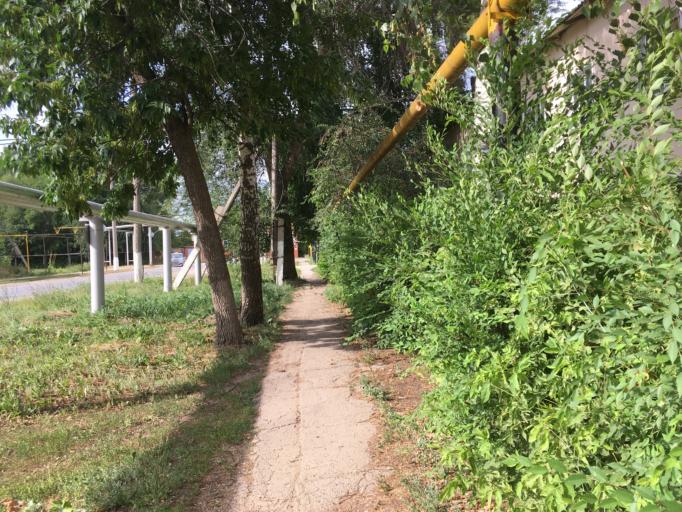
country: RU
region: Samara
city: Bezenchuk
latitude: 52.9876
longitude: 49.4410
